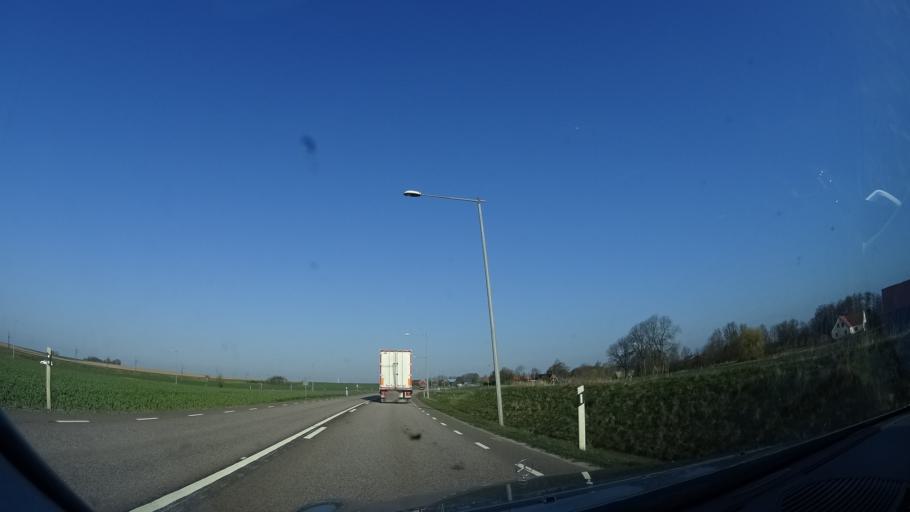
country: SE
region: Skane
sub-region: Eslovs Kommun
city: Eslov
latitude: 55.8540
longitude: 13.2771
